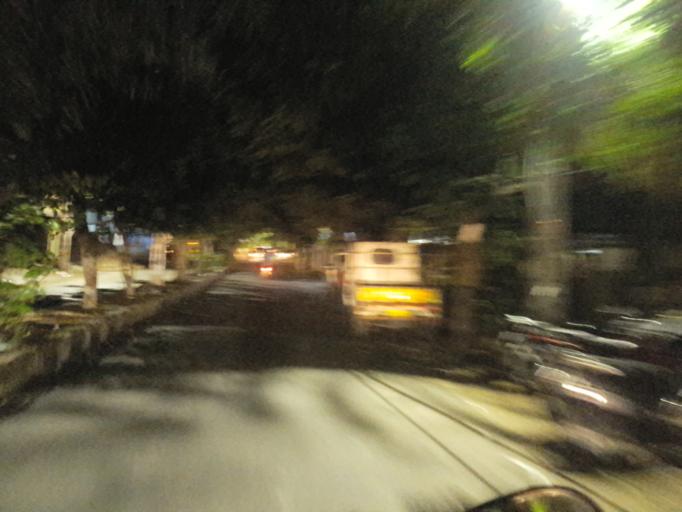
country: IN
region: Telangana
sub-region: Rangareddi
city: Kukatpalli
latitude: 17.4795
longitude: 78.3930
